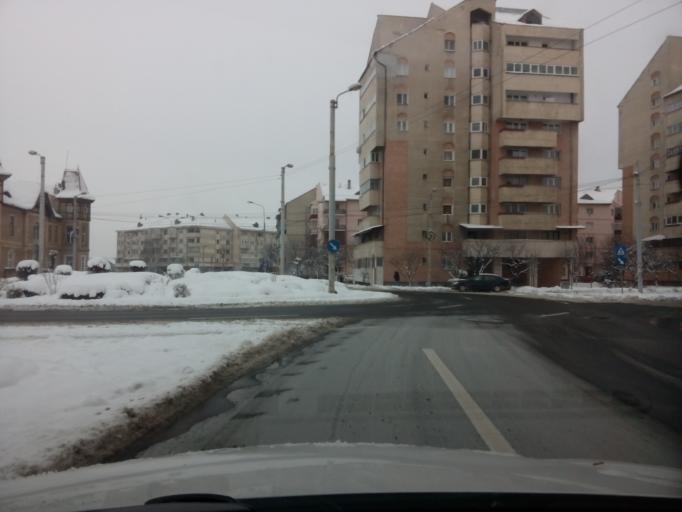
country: RO
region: Sibiu
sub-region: Municipiul Sibiu
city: Sibiu
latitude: 45.8012
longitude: 24.1569
